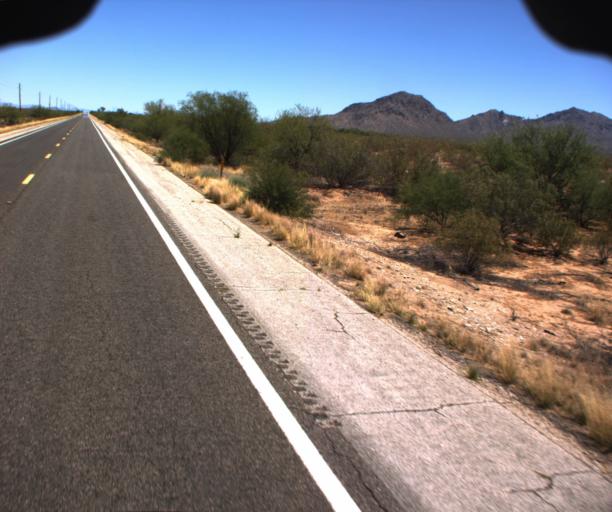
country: US
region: Arizona
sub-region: La Paz County
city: Salome
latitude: 33.8967
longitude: -113.3167
